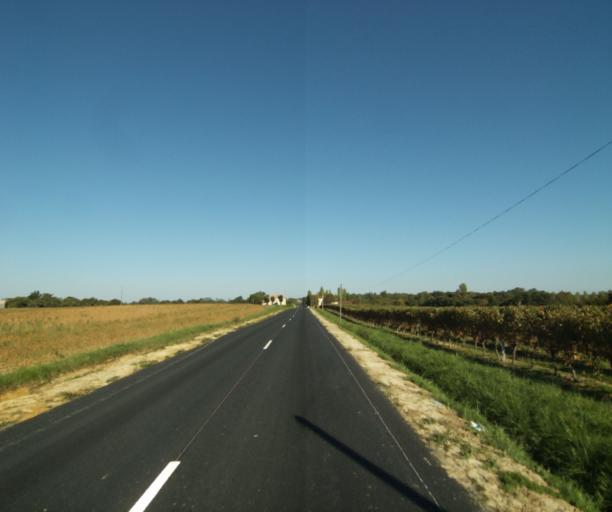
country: FR
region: Midi-Pyrenees
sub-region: Departement du Gers
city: Cazaubon
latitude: 43.9048
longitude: -0.0182
